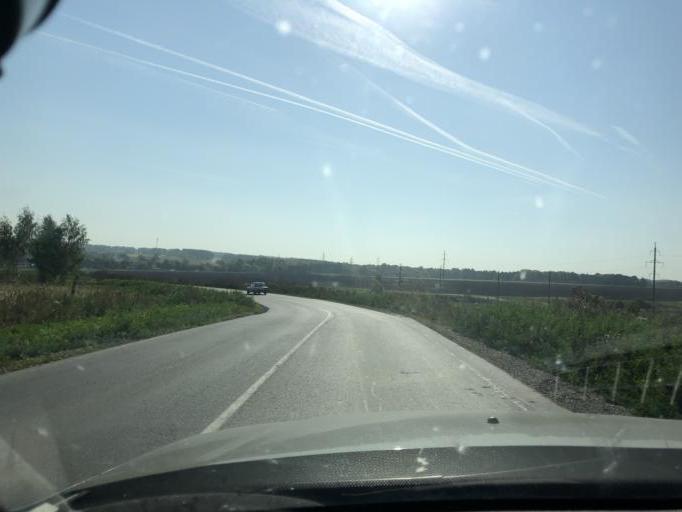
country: RU
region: Tula
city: Yasnogorsk
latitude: 54.4658
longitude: 37.6854
